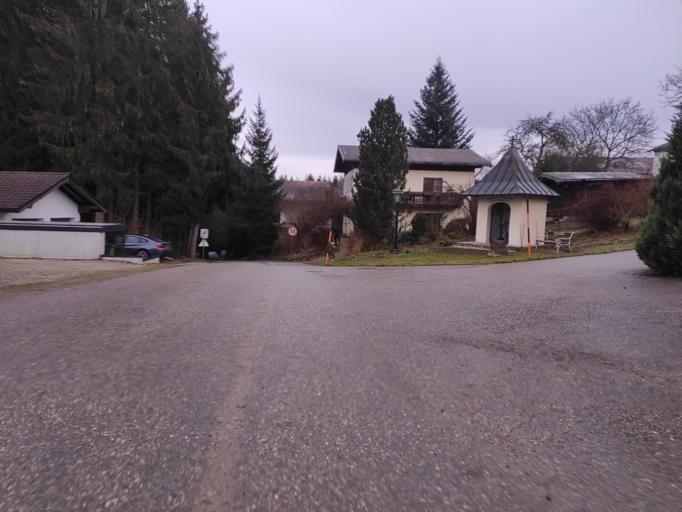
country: AT
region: Salzburg
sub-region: Politischer Bezirk Salzburg-Umgebung
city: Obertrum am See
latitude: 47.9134
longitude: 13.0694
